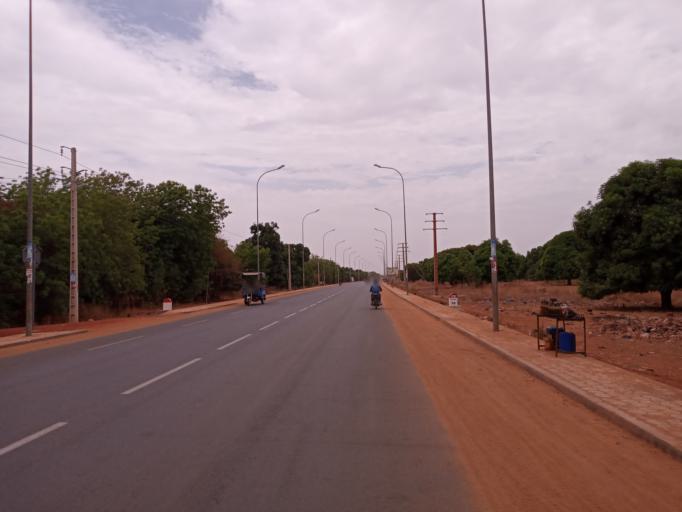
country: ML
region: Koulikoro
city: Koulikoro
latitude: 12.8504
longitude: -7.5727
